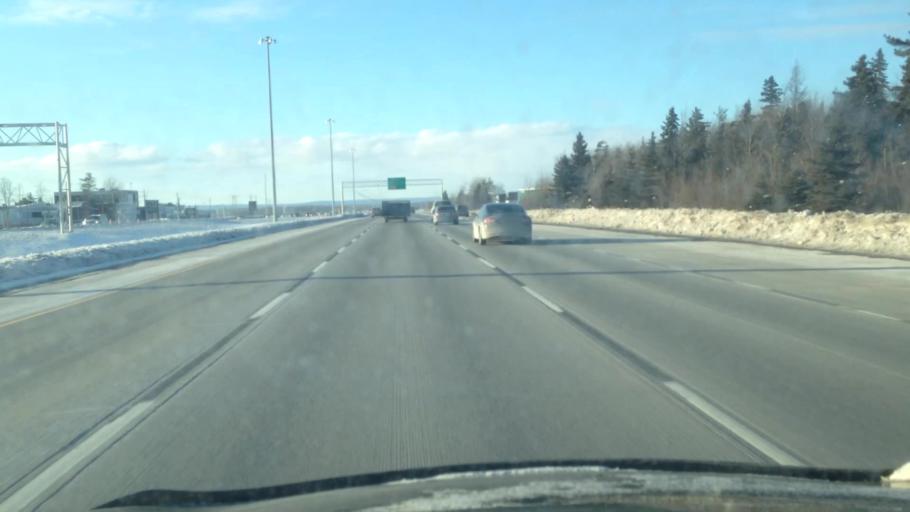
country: CA
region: Quebec
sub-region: Laurentides
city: Blainville
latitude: 45.6823
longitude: -73.9212
